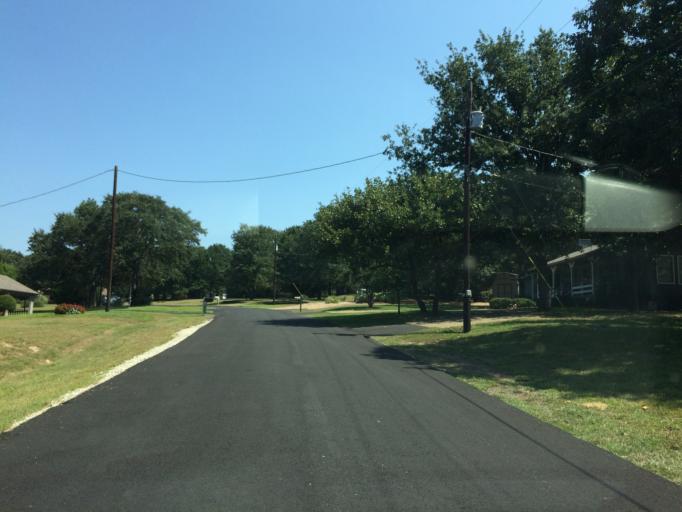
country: US
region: Texas
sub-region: Wood County
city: Hawkins
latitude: 32.7180
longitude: -95.1779
